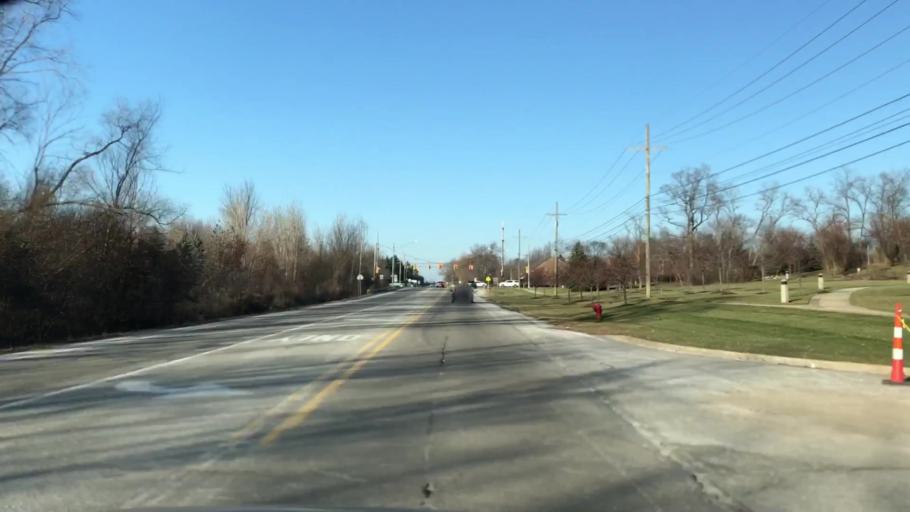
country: US
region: Michigan
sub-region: Oakland County
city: Novi
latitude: 42.4640
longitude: -83.4944
